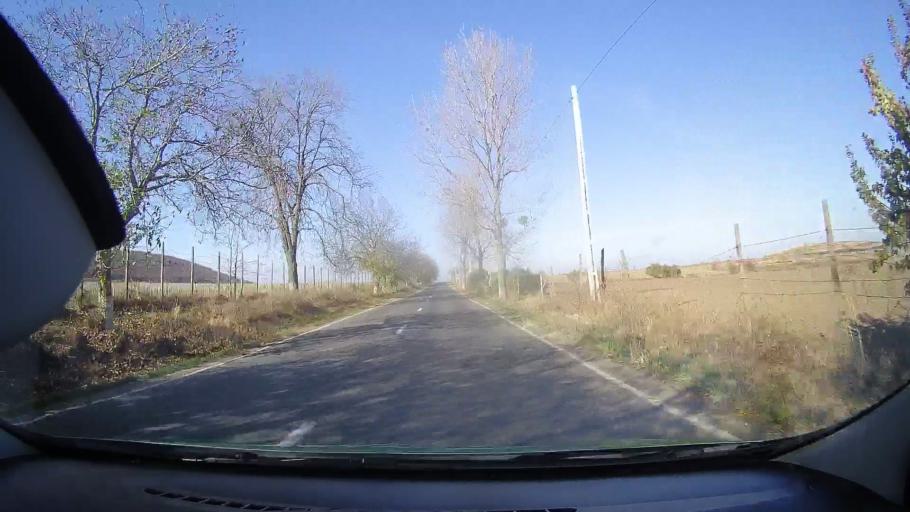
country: RO
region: Tulcea
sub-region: Oras Babadag
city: Babadag
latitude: 44.8819
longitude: 28.7435
